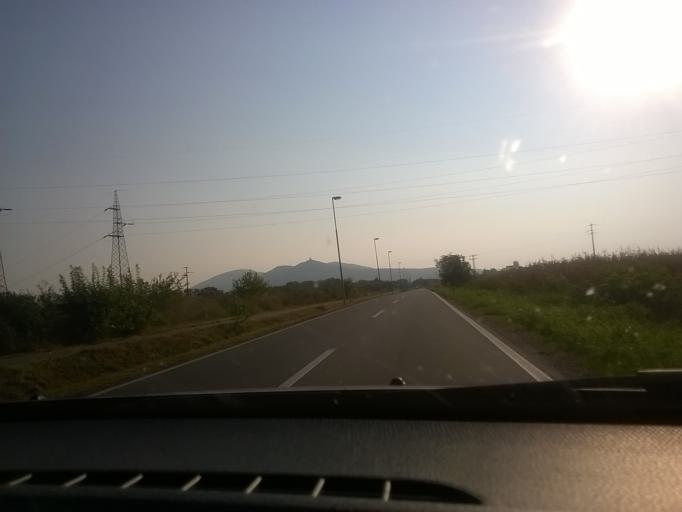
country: RS
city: Pavlis
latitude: 45.1124
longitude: 21.2677
